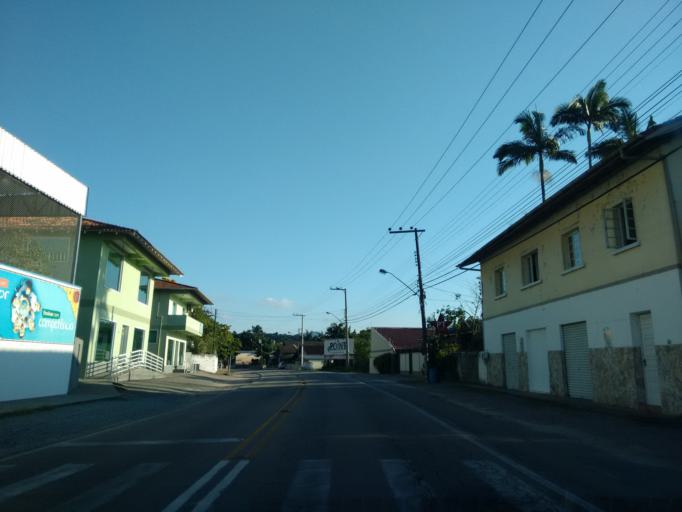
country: BR
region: Santa Catarina
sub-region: Gaspar
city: Gaspar
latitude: -26.9247
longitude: -48.9518
